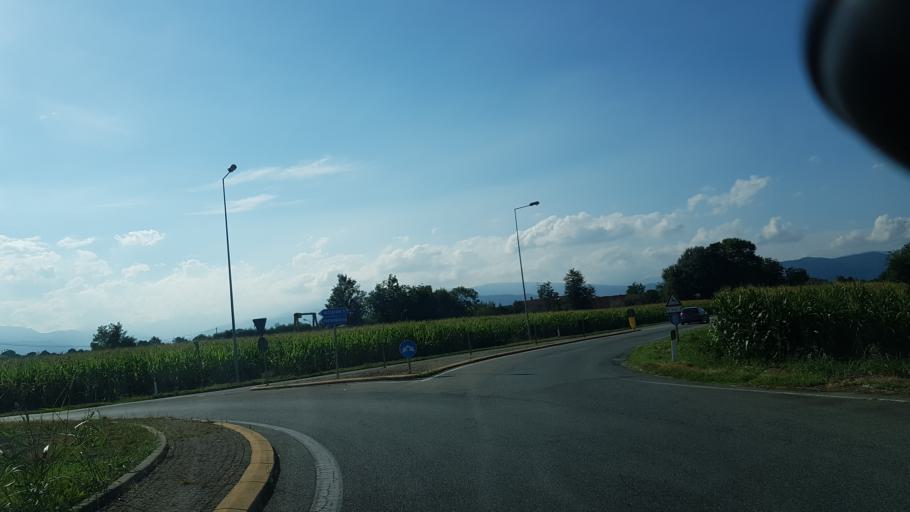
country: IT
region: Piedmont
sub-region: Provincia di Cuneo
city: Roata Rossi
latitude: 44.4476
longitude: 7.5276
